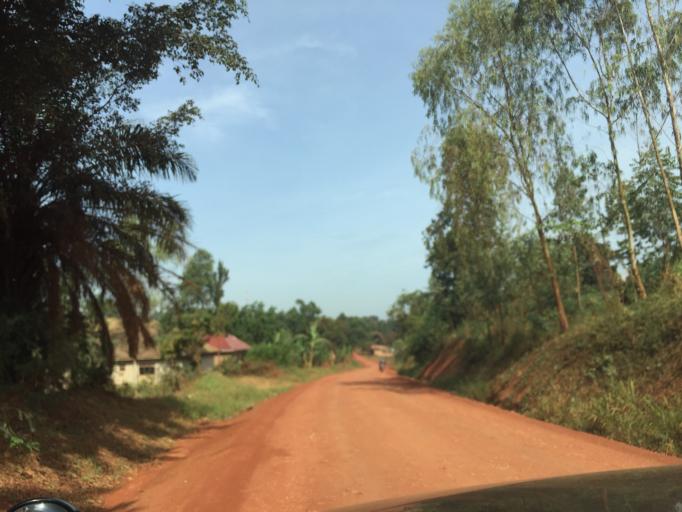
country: UG
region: Central Region
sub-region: Wakiso District
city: Wakiso
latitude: 0.4626
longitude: 32.5481
